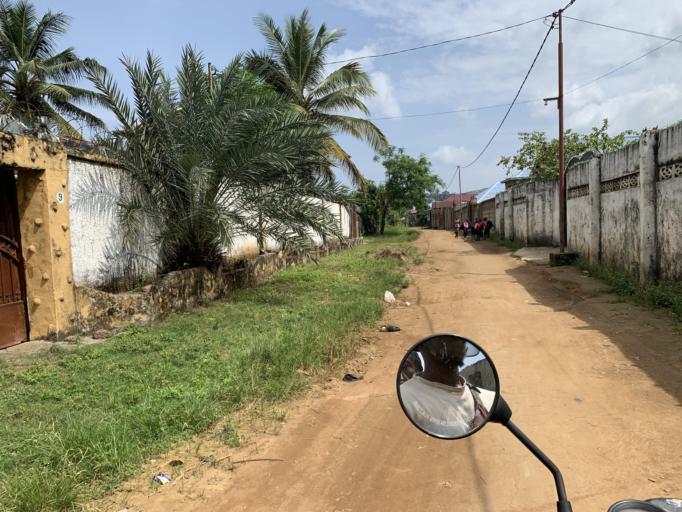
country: SL
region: Western Area
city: Hastings
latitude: 8.3898
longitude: -13.1381
